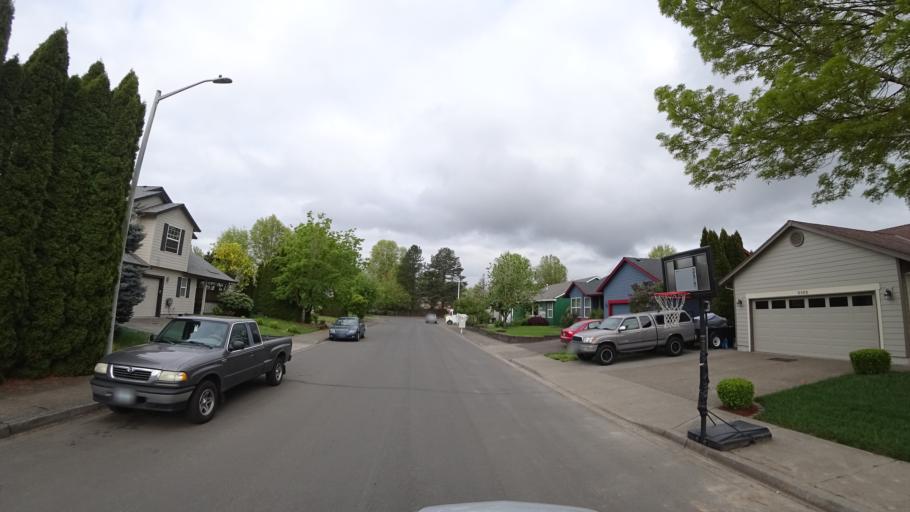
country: US
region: Oregon
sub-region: Washington County
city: Hillsboro
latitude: 45.5339
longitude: -122.9596
